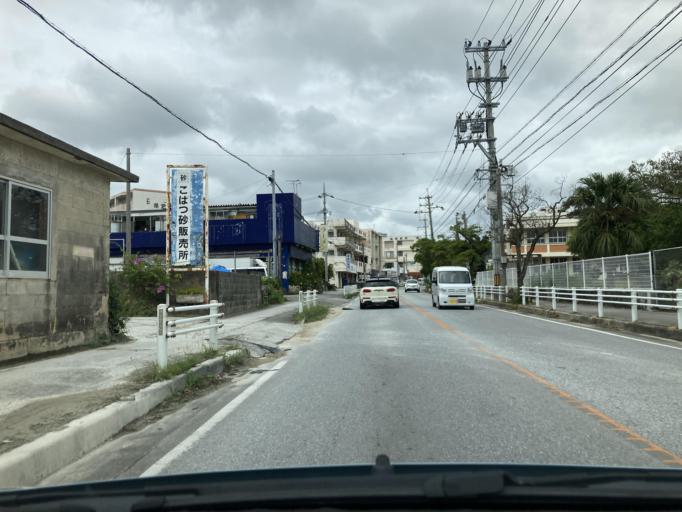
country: JP
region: Okinawa
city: Ginowan
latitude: 26.2276
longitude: 127.7550
